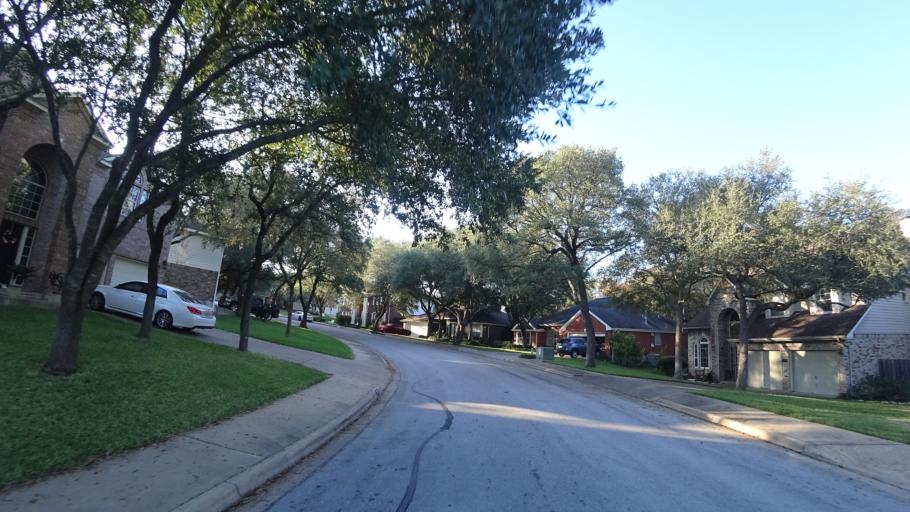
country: US
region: Texas
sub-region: Travis County
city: Hudson Bend
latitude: 30.3742
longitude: -97.8884
